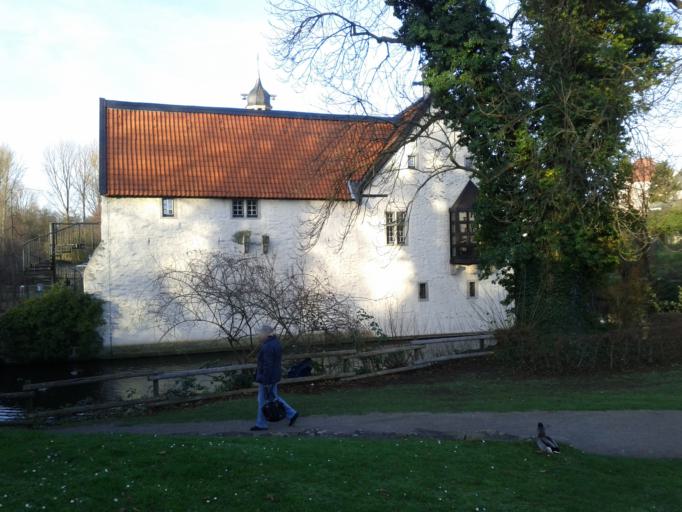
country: DE
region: North Rhine-Westphalia
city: Schwerte
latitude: 51.4926
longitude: 7.5543
